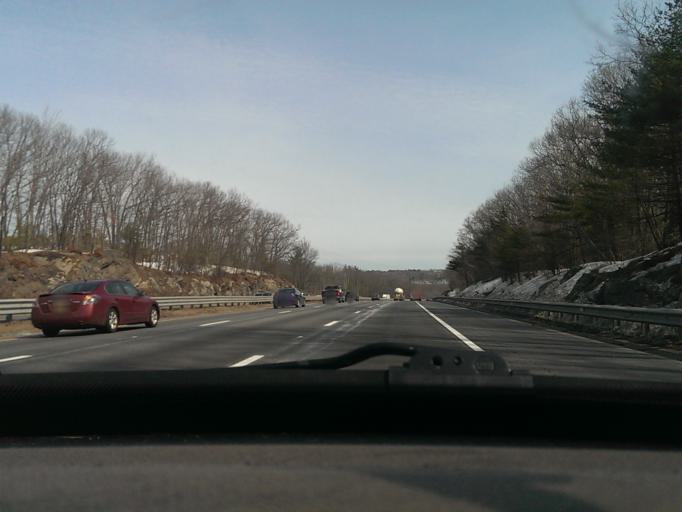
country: US
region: Massachusetts
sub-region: Worcester County
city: Auburn
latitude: 42.2051
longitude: -71.8085
